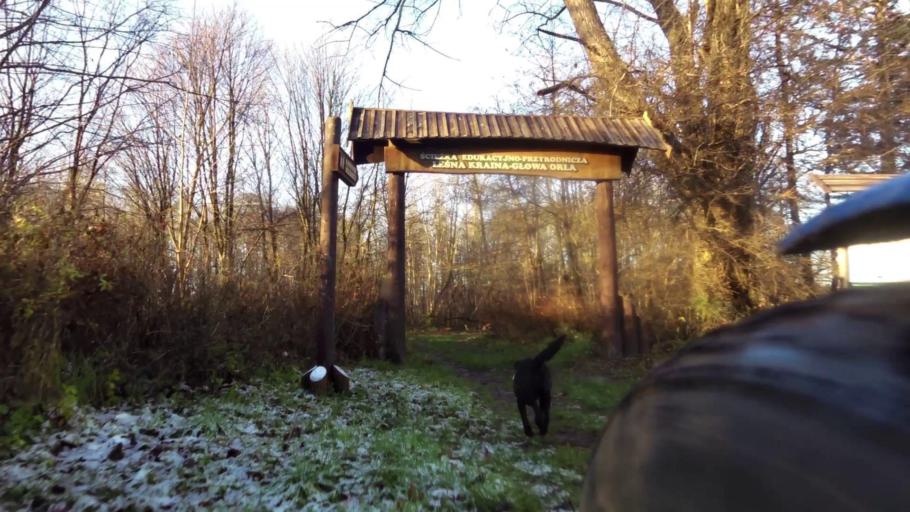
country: PL
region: West Pomeranian Voivodeship
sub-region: Powiat szczecinecki
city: Borne Sulinowo
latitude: 53.5895
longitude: 16.5363
